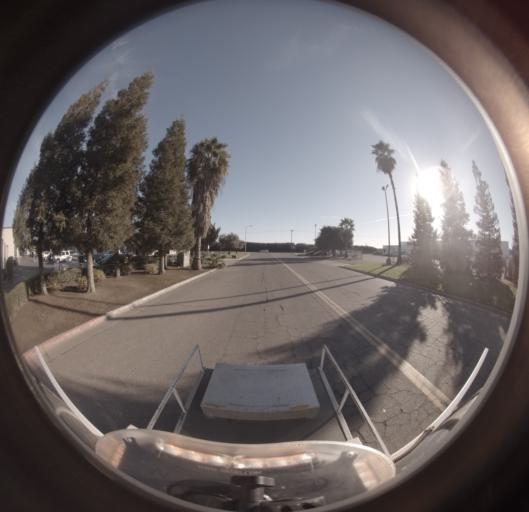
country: US
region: California
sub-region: Monterey County
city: King City
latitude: 36.1085
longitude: -120.9157
